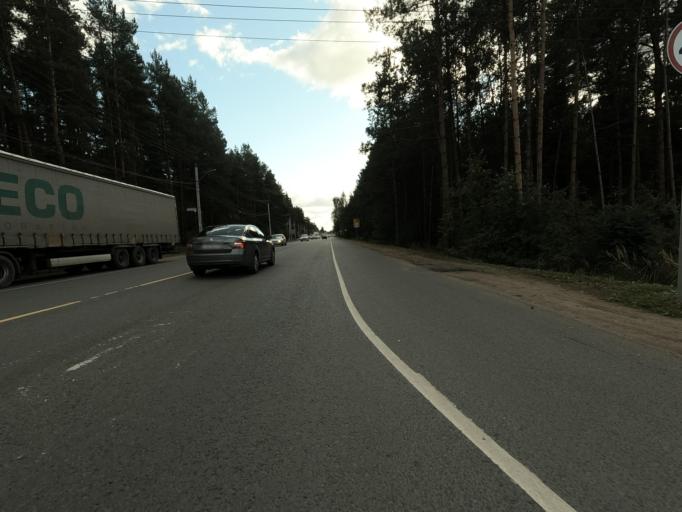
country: RU
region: Leningrad
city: Vsevolozhsk
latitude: 59.9942
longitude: 30.6592
